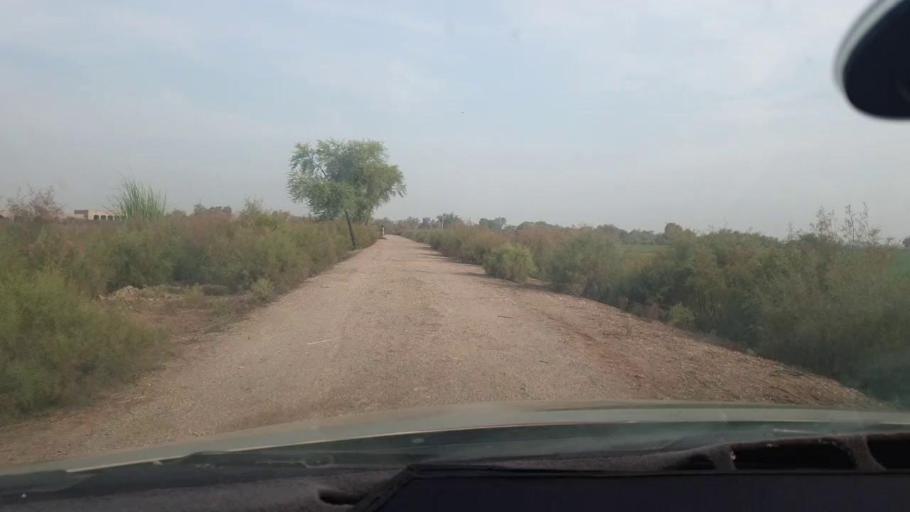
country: PK
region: Balochistan
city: Jhatpat
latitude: 28.3691
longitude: 68.4043
